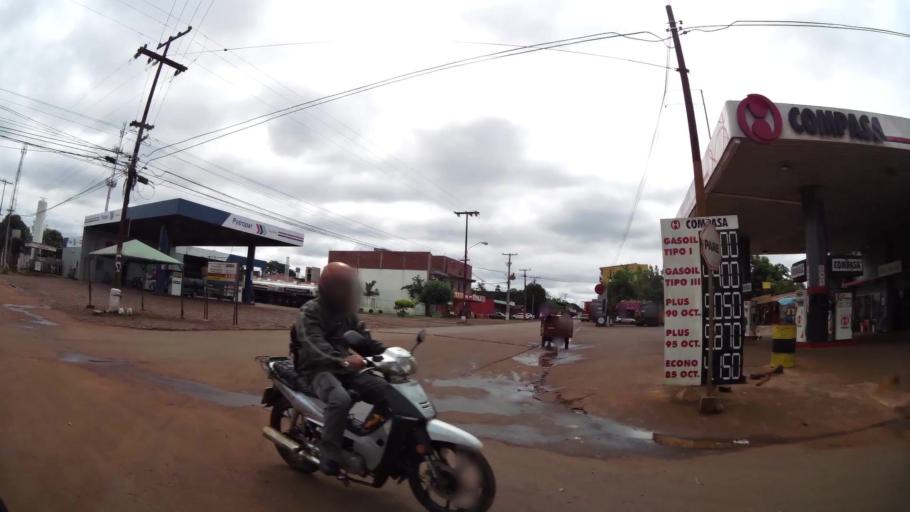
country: PY
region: Alto Parana
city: Ciudad del Este
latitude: -25.3890
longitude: -54.6462
